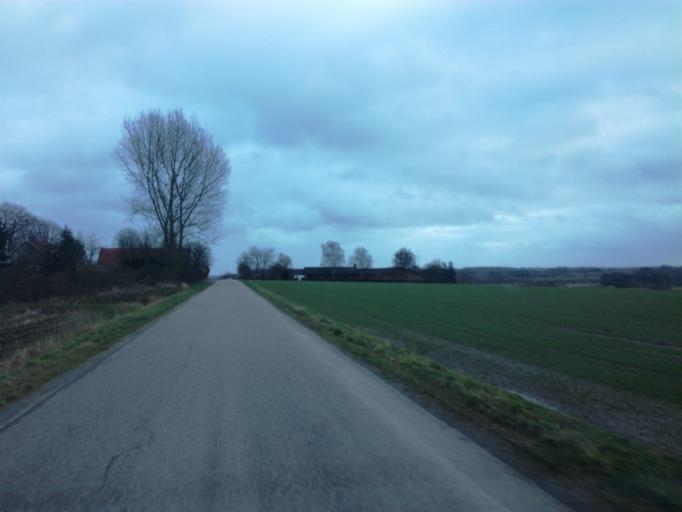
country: DK
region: South Denmark
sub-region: Vejle Kommune
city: Brejning
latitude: 55.6242
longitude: 9.7264
